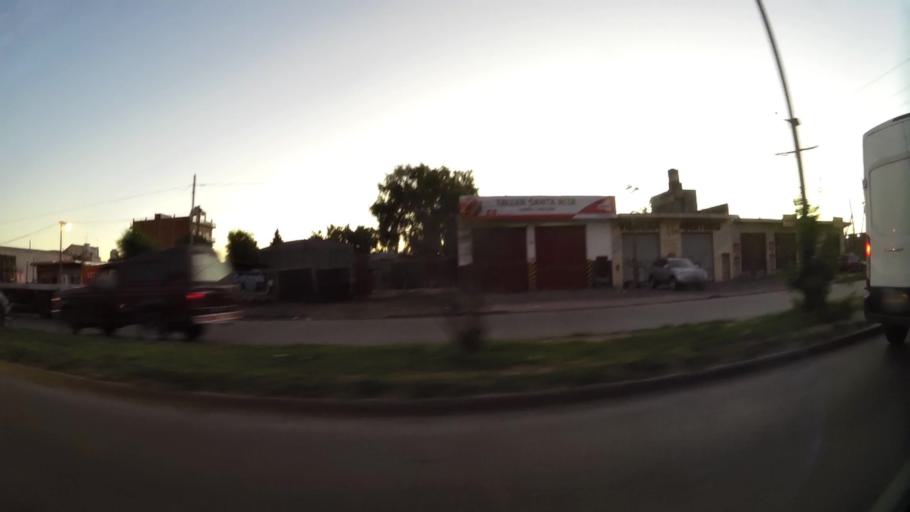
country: AR
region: Buenos Aires
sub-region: Partido de Moron
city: Moron
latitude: -34.7074
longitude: -58.6129
